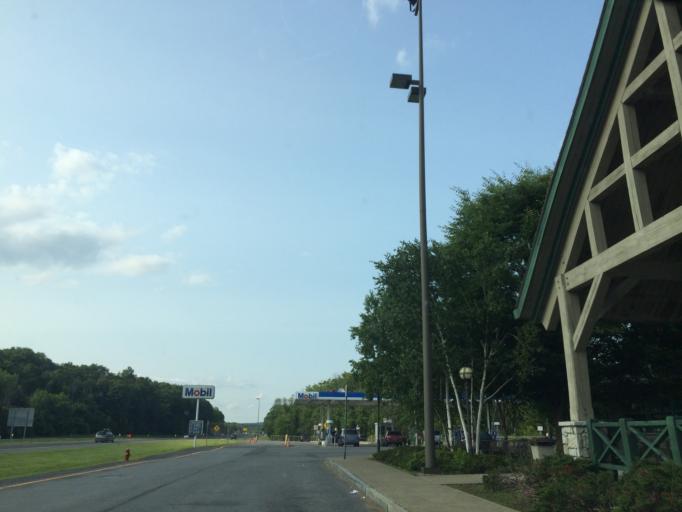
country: US
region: New York
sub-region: Ulster County
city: Saugerties
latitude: 42.1106
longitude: -73.9571
